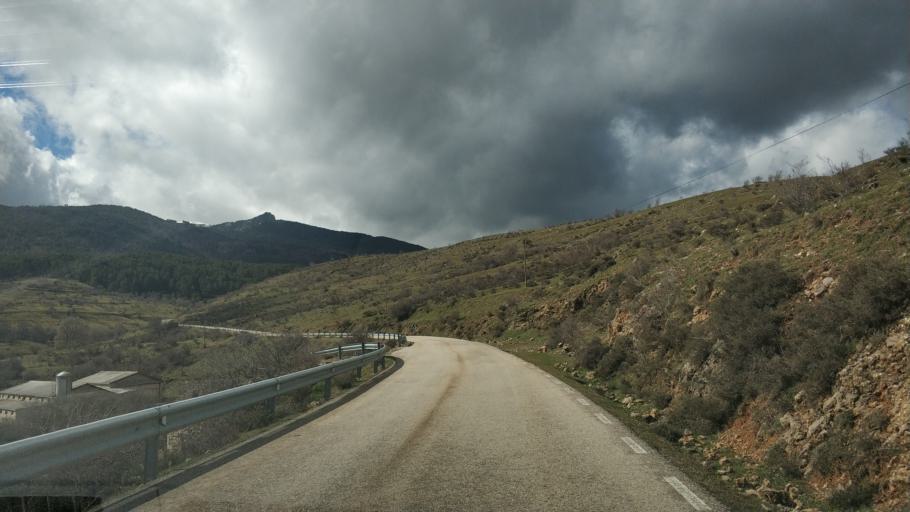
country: ES
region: Castille and Leon
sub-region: Provincia de Burgos
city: Neila
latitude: 42.0584
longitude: -3.0032
